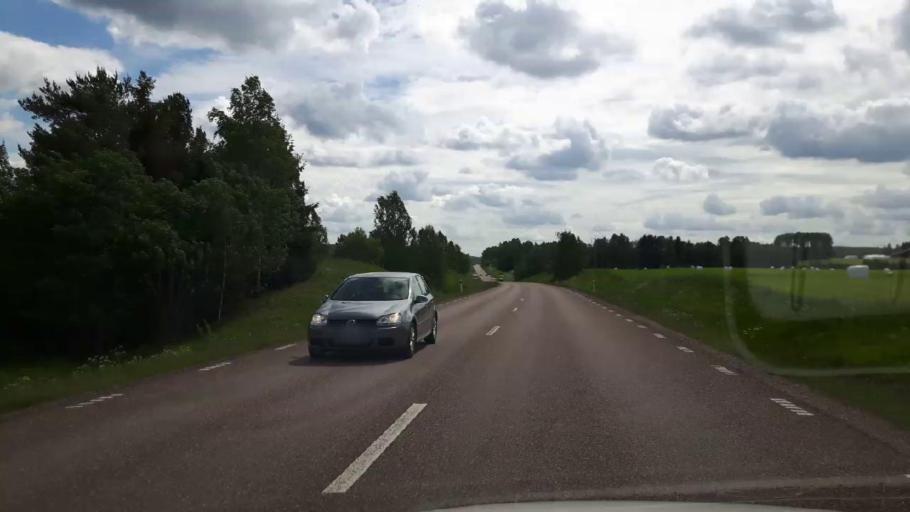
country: SE
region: Dalarna
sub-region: Hedemora Kommun
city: Langshyttan
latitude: 60.3853
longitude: 15.9055
